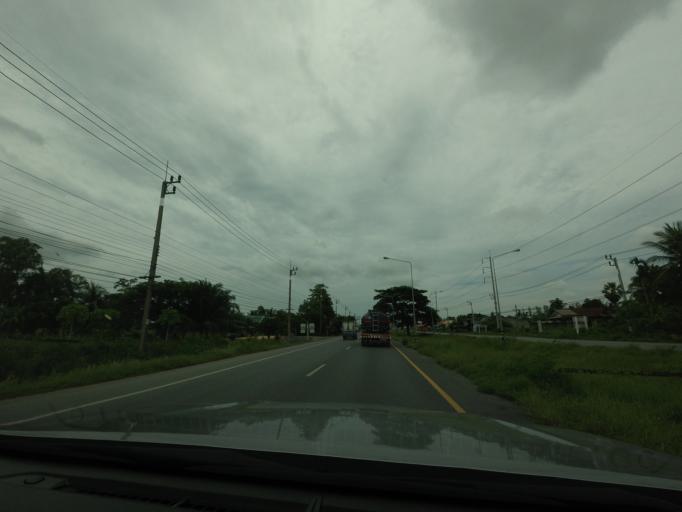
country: TH
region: Nakhon Si Thammarat
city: Hua Sai
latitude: 8.0469
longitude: 100.2781
